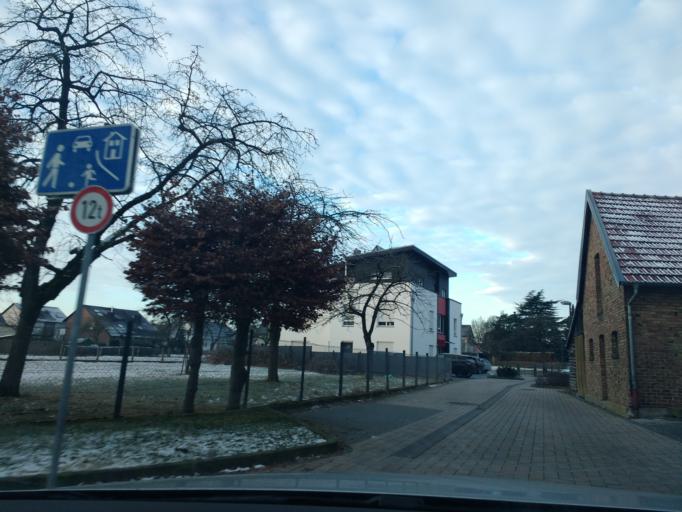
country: DE
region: North Rhine-Westphalia
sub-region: Regierungsbezirk Detmold
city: Paderborn
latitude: 51.7302
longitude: 8.6906
